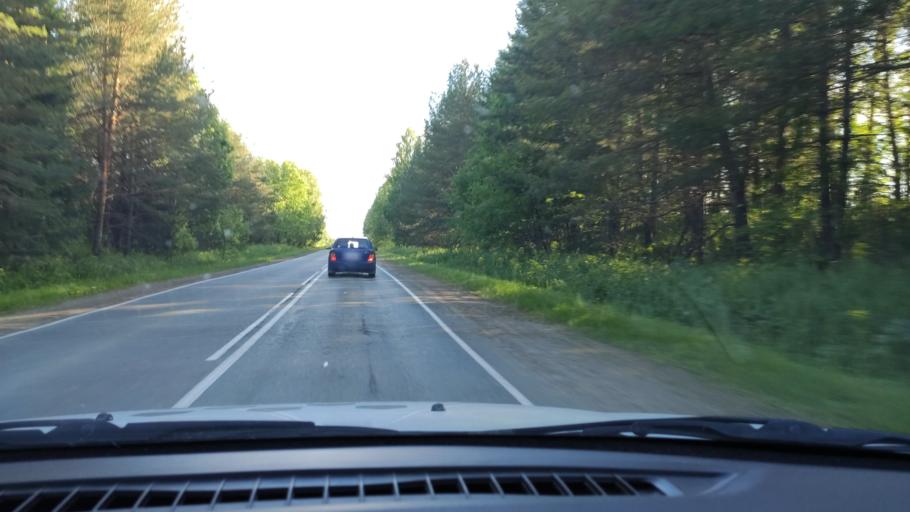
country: RU
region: Perm
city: Kungur
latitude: 57.3668
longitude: 56.8268
